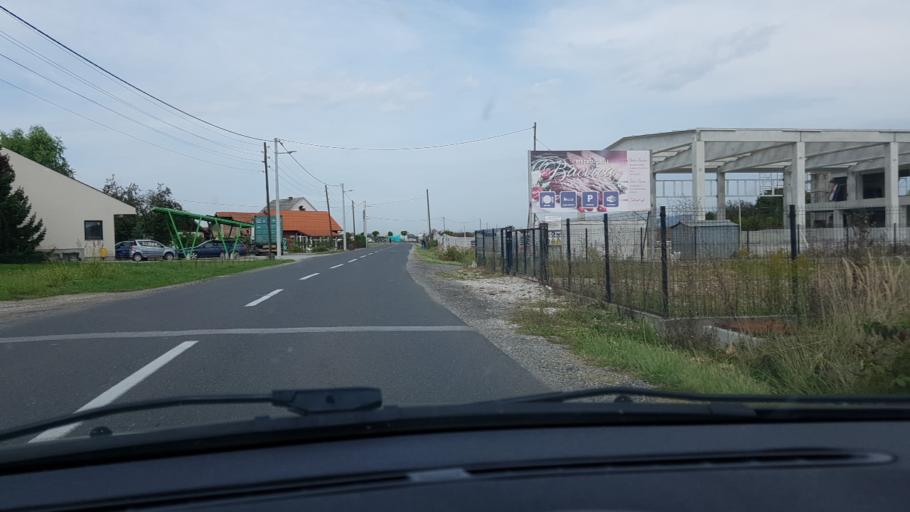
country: HR
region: Grad Zagreb
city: Lucko
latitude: 45.7621
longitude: 15.8712
